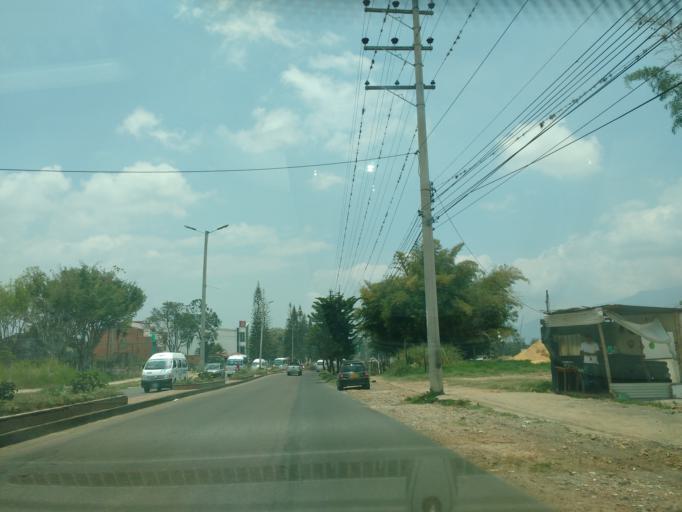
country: CO
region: Cundinamarca
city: Fusagasuga
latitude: 4.3320
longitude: -74.3744
